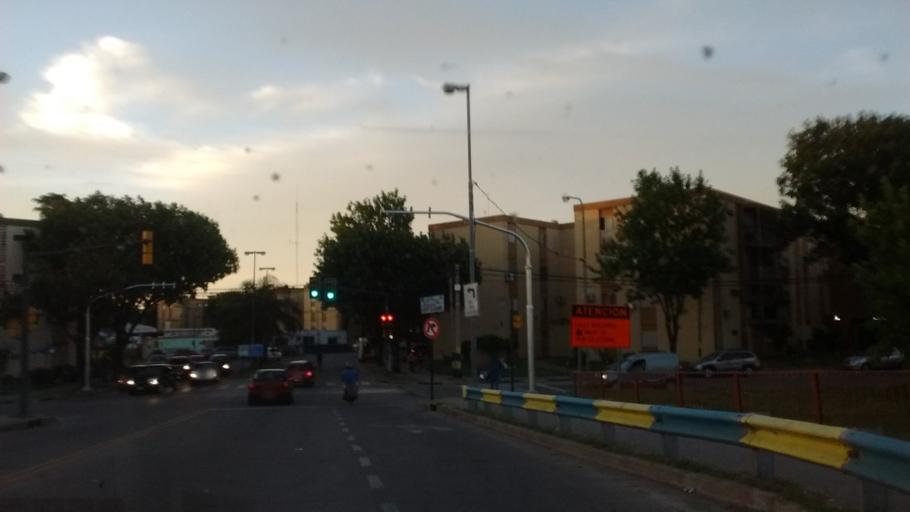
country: AR
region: Santa Fe
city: Granadero Baigorria
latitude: -32.8876
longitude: -60.7151
